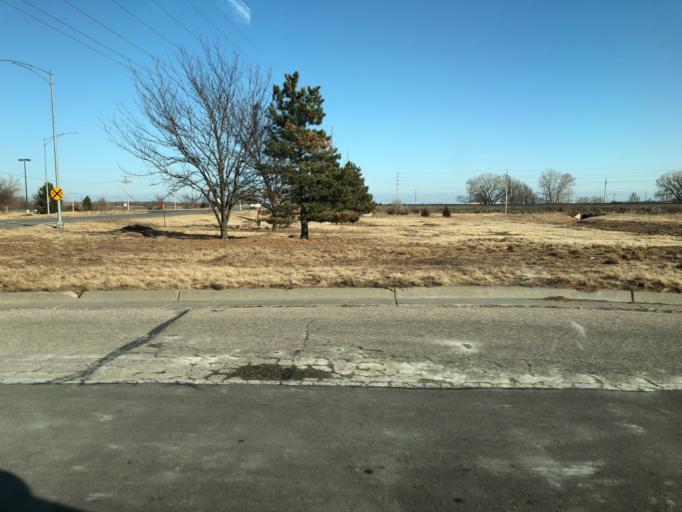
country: US
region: Kansas
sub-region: Reno County
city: Hutchinson
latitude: 38.0721
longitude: -97.8913
